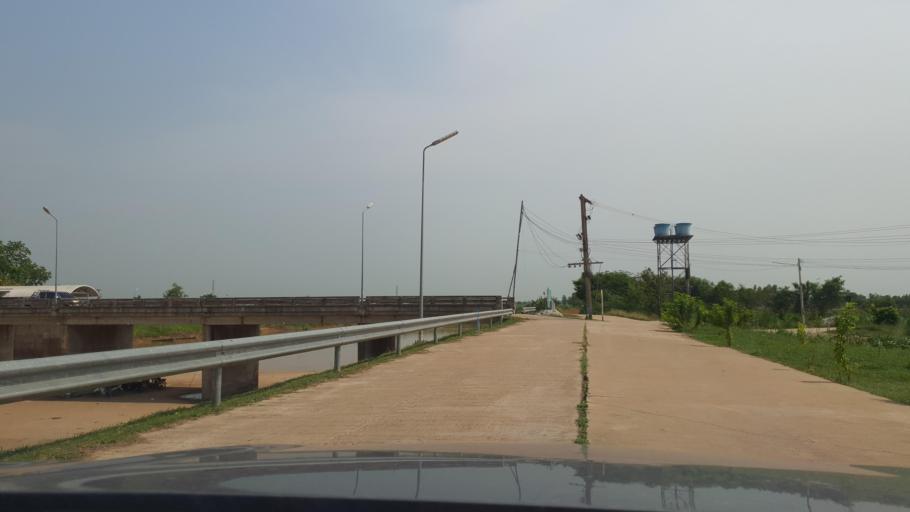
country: TH
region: Phitsanulok
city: Bang Rakam
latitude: 16.7641
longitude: 100.1182
